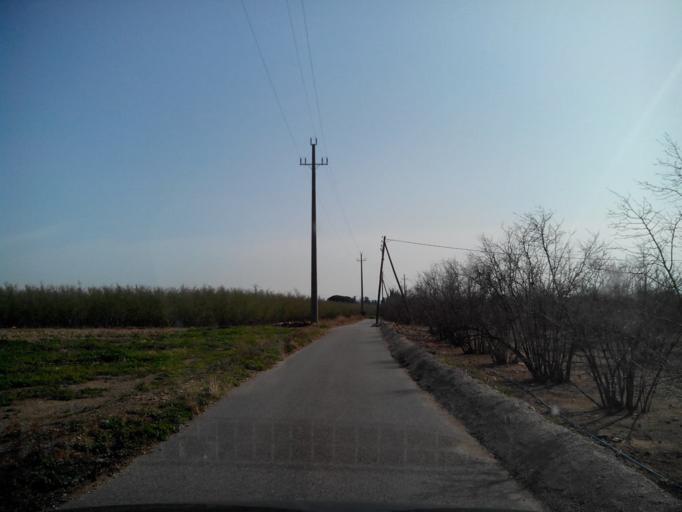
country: ES
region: Catalonia
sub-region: Provincia de Tarragona
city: La Selva
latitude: 41.2120
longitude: 1.1691
